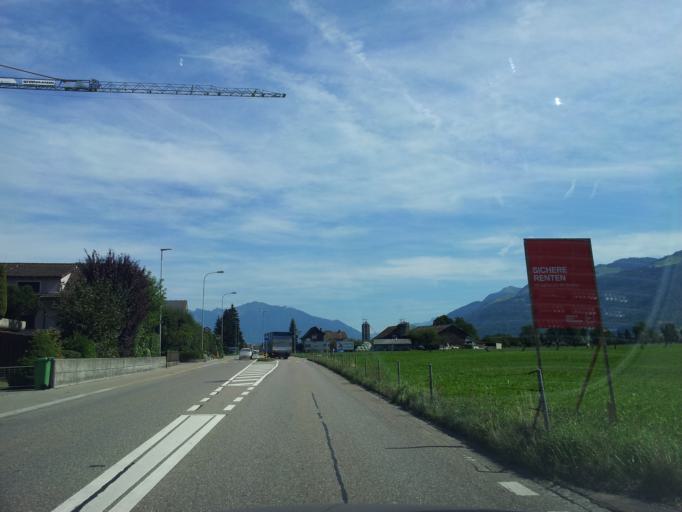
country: CH
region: Schwyz
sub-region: Bezirk March
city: Lachen
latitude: 47.1921
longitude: 8.8811
